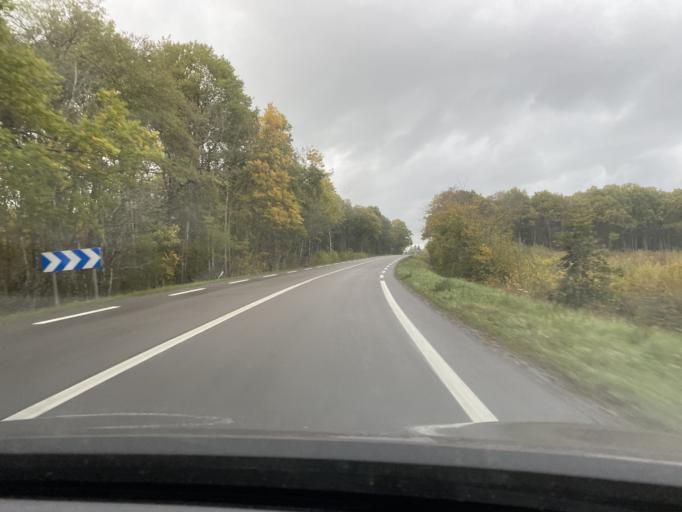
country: FR
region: Bourgogne
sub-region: Departement de la Cote-d'Or
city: Saulieu
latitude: 47.3343
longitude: 4.1927
